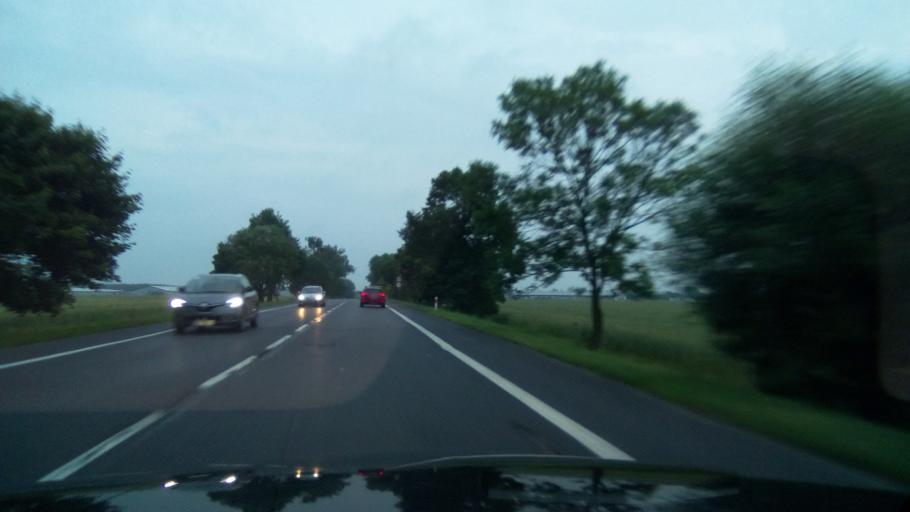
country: PL
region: Greater Poland Voivodeship
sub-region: Powiat poznanski
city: Kobylnica
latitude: 52.4646
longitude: 17.1377
